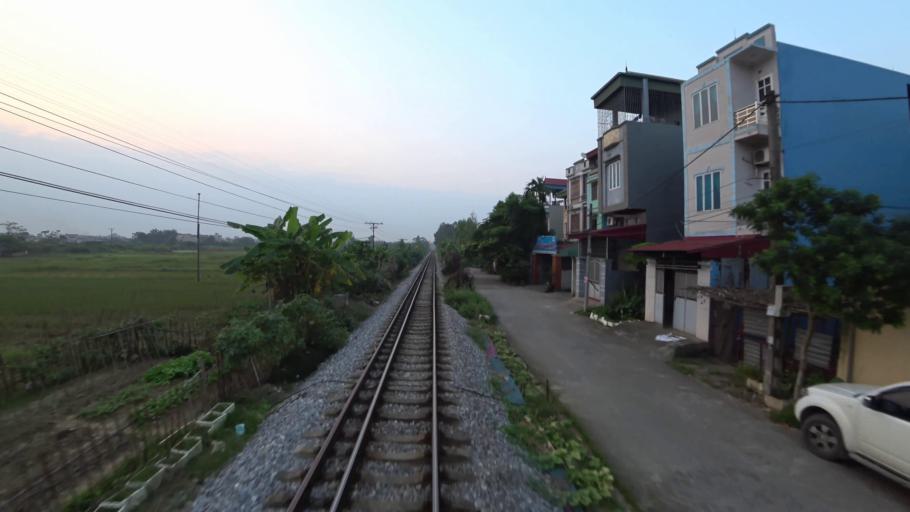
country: VN
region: Ha Noi
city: Dong Anh
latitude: 21.1491
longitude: 105.8572
